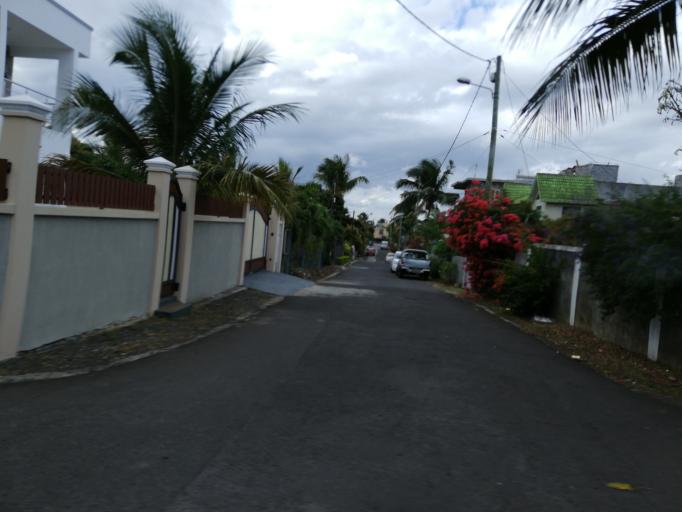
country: MU
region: Black River
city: Gros Cailloux
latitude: -20.2330
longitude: 57.4540
